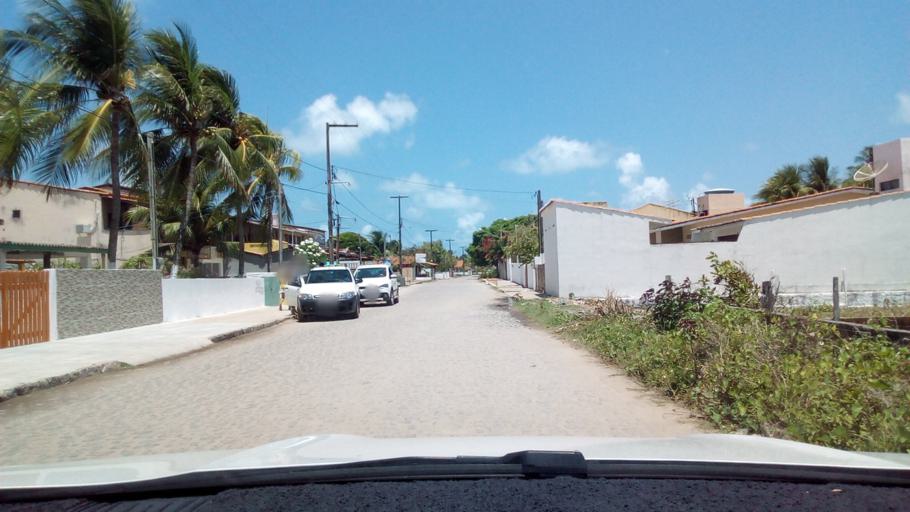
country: BR
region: Paraiba
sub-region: Pitimbu
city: Pitimbu
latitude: -7.5165
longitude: -34.8131
